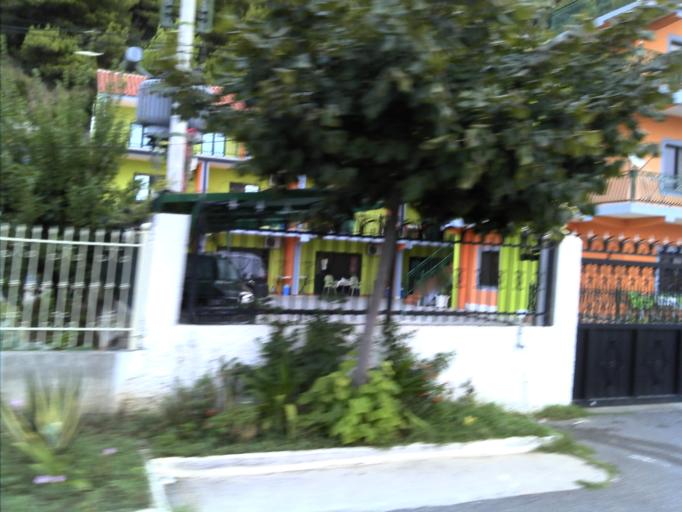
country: AL
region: Lezhe
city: Shengjin
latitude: 41.8084
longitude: 19.6041
